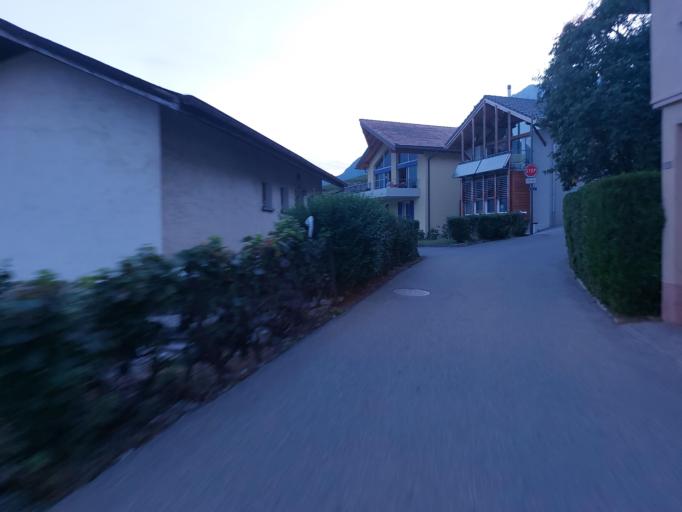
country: CH
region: Valais
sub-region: Conthey District
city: Conthey
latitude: 46.2397
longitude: 7.3062
